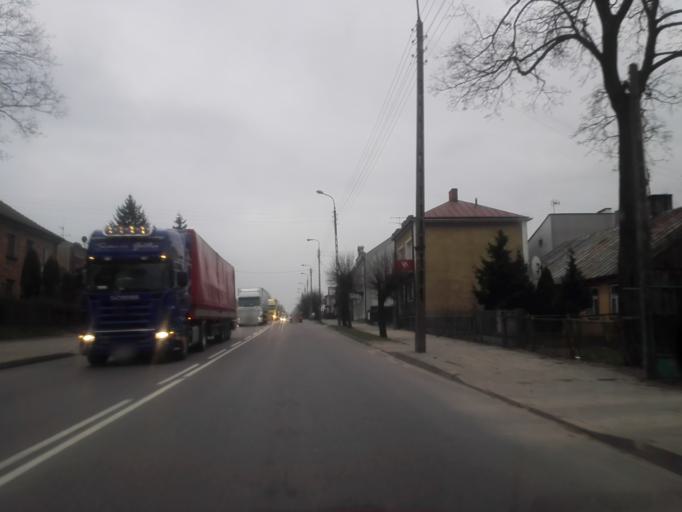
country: PL
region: Podlasie
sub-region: Powiat grajewski
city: Grajewo
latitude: 53.6453
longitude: 22.4510
